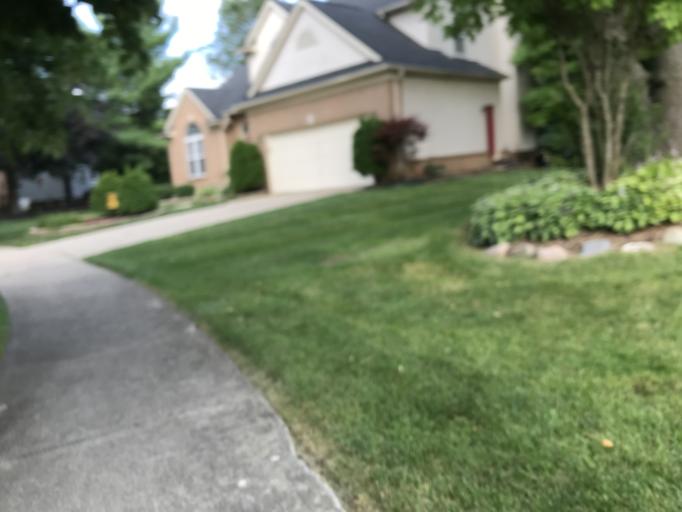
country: US
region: Michigan
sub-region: Oakland County
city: Franklin
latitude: 42.4983
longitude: -83.3343
